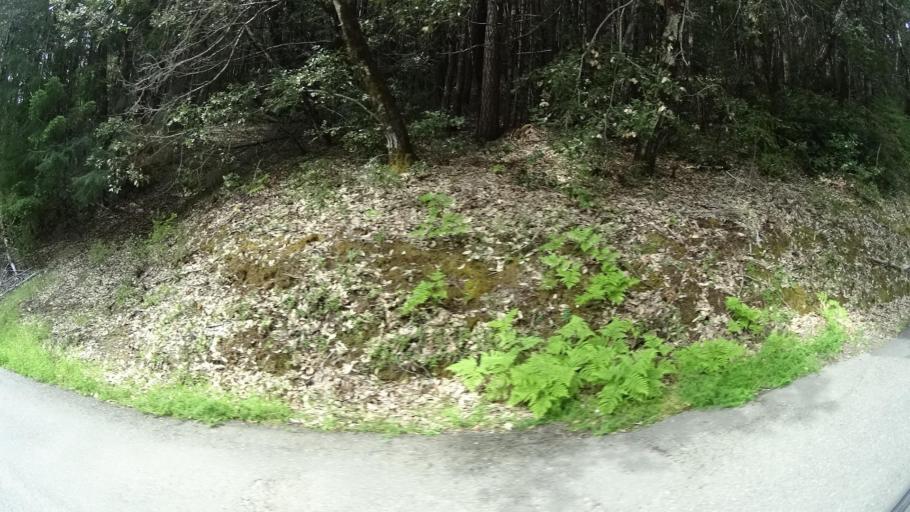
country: US
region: California
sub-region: Humboldt County
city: Redway
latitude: 40.0631
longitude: -123.8288
